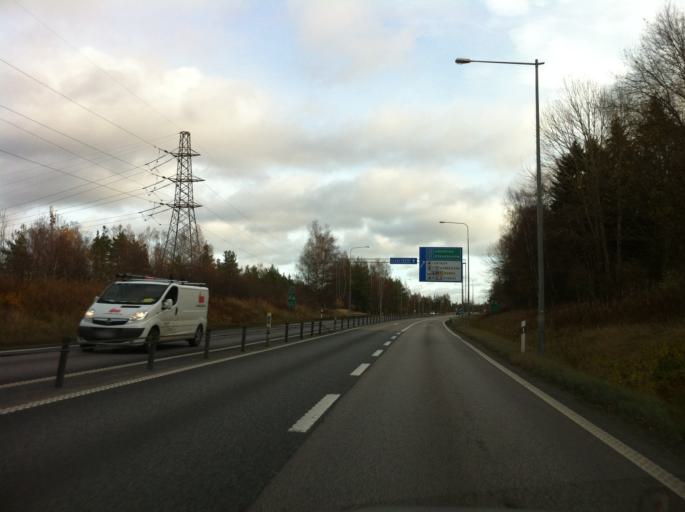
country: SE
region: Kronoberg
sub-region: Vaxjo Kommun
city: Gemla
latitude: 56.8420
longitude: 14.7110
